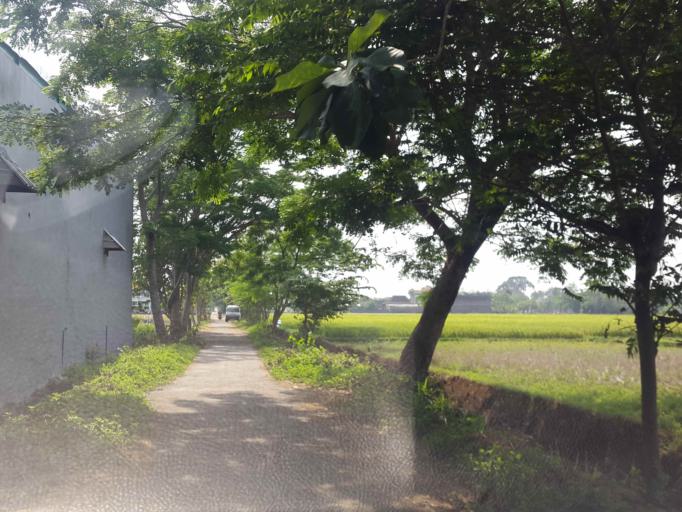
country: ID
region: Central Java
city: Jaten
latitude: -7.5798
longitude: 110.9378
